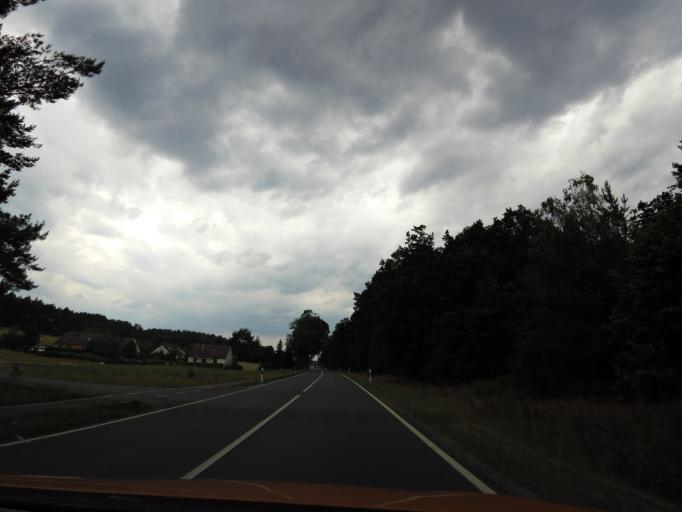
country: DE
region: Brandenburg
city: Baruth
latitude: 52.0381
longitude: 13.5178
